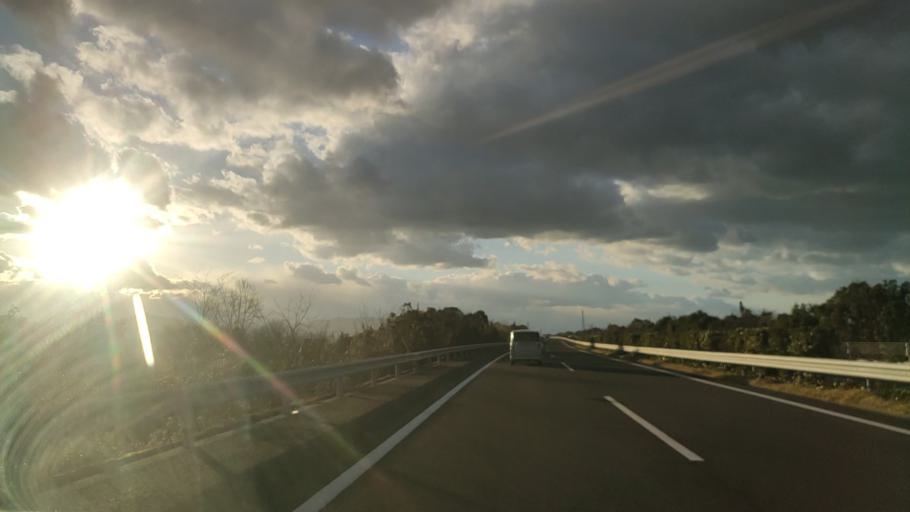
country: JP
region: Ehime
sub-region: Shikoku-chuo Shi
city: Matsuyama
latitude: 33.7860
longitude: 132.8704
